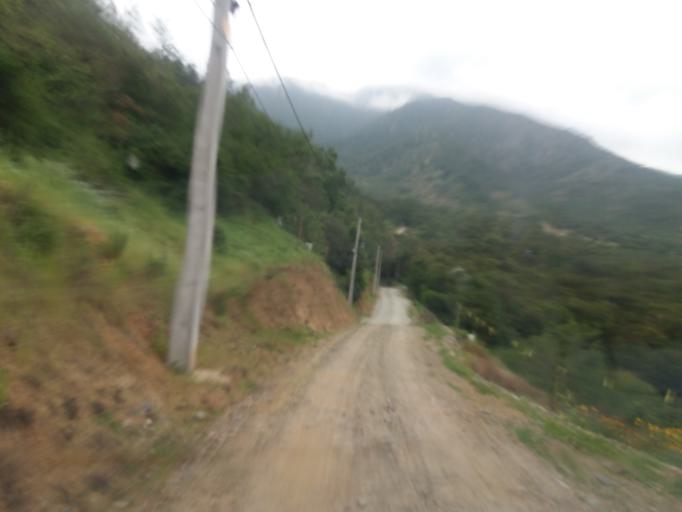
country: CL
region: Valparaiso
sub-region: Provincia de Marga Marga
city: Limache
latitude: -33.0239
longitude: -71.1314
